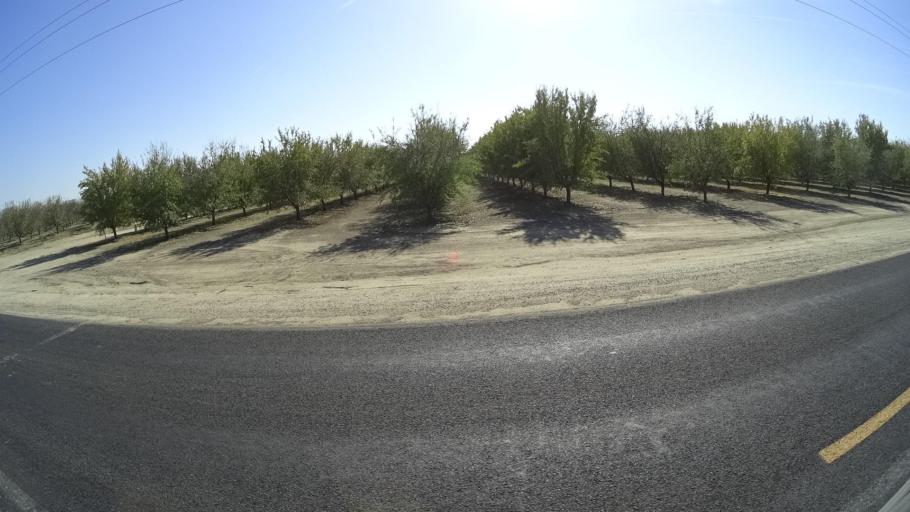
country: US
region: California
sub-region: Kern County
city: McFarland
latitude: 35.6455
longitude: -119.2459
